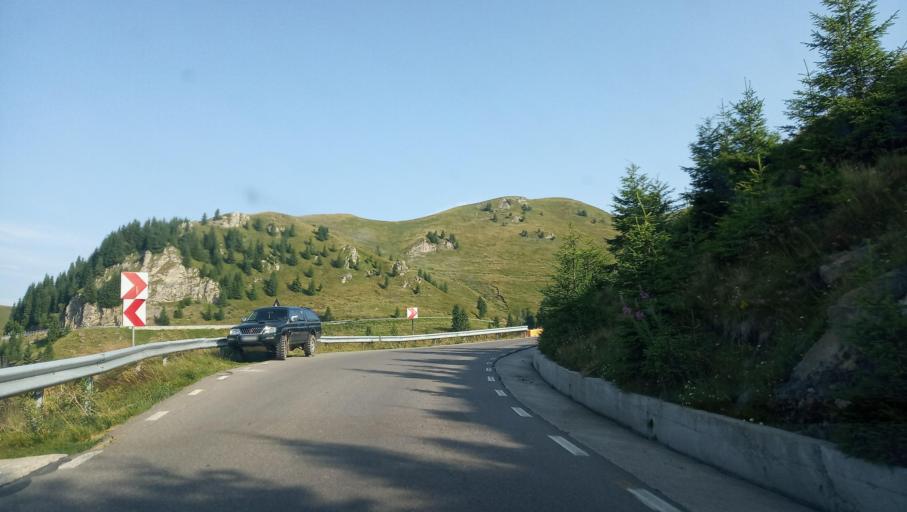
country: RO
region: Prahova
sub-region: Oras Sinaia
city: Sinaia
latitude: 45.3207
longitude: 25.4772
